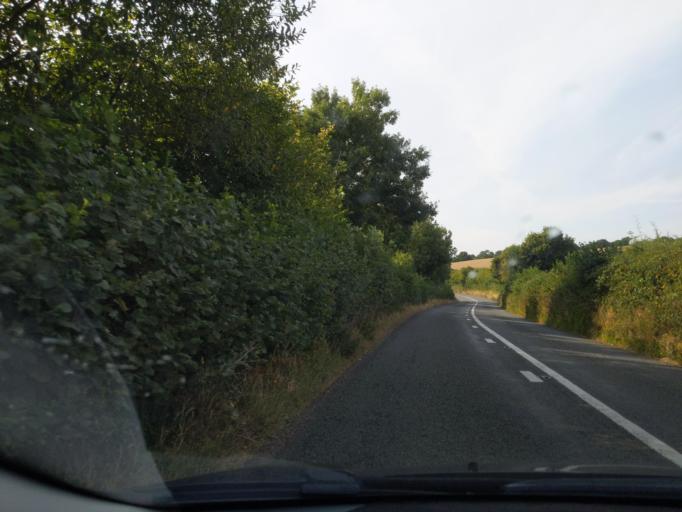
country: GB
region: England
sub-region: Devon
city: Winkleigh
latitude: 50.9028
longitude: -3.8829
